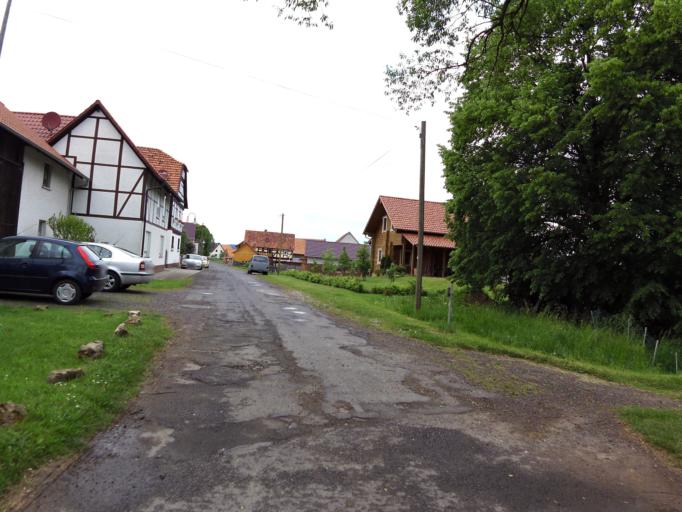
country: DE
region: Thuringia
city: Dippach
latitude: 50.9227
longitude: 10.0841
